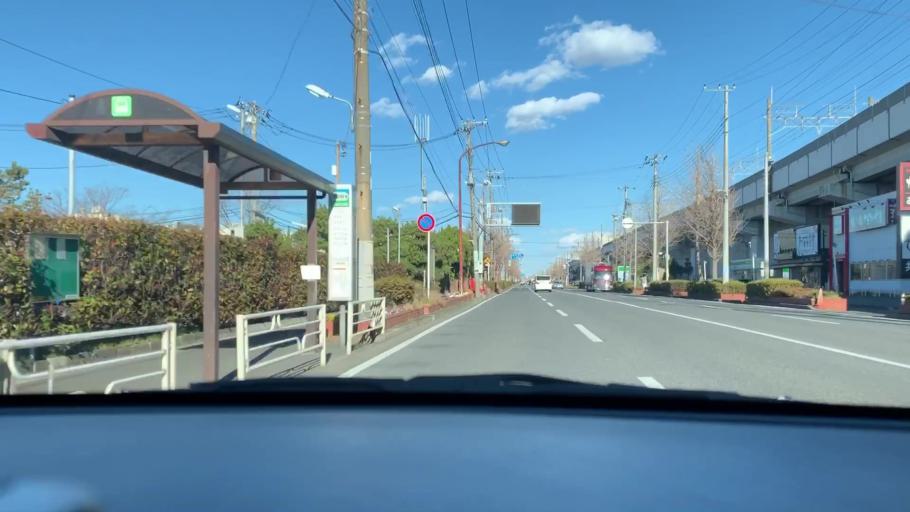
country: JP
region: Tokyo
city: Urayasu
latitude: 35.6365
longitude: 139.8963
